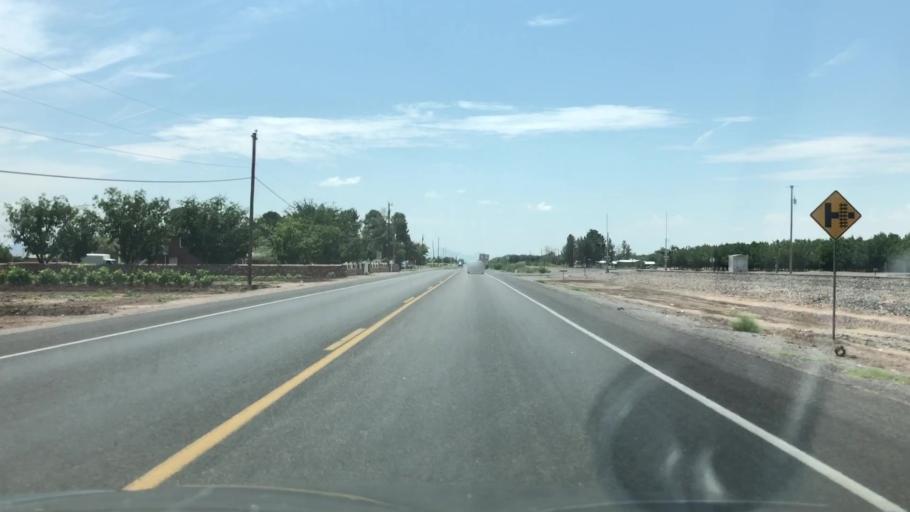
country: US
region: New Mexico
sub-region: Dona Ana County
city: Mesquite
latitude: 32.1808
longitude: -106.7069
